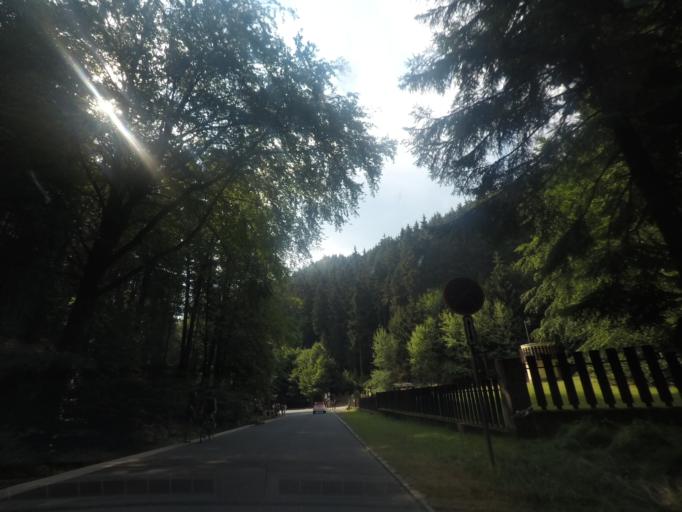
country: DE
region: Saxony
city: Sebnitz
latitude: 50.8807
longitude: 14.2711
